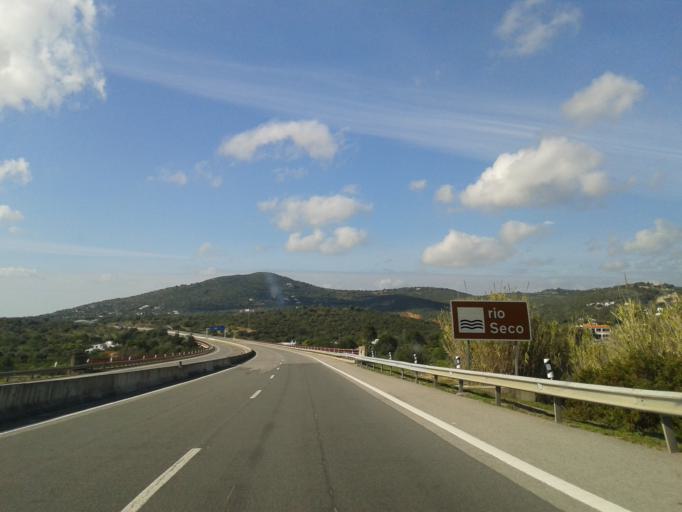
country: PT
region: Faro
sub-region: Sao Bras de Alportel
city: Sao Bras de Alportel
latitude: 37.0997
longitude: -7.9006
